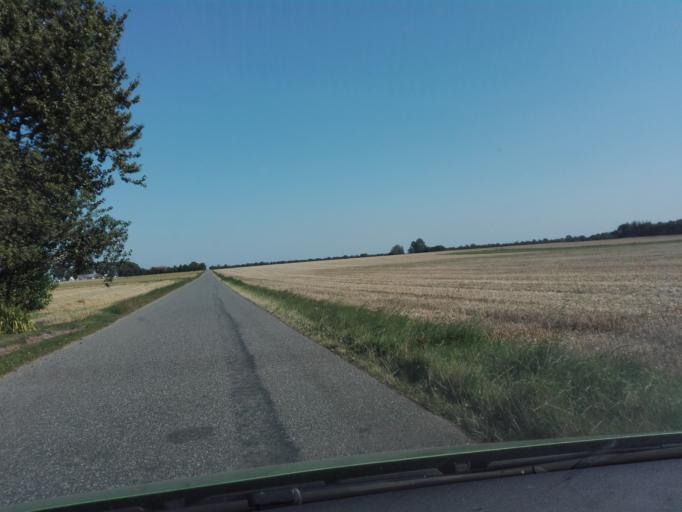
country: DK
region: Central Jutland
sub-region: Odder Kommune
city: Odder
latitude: 55.9391
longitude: 10.2451
